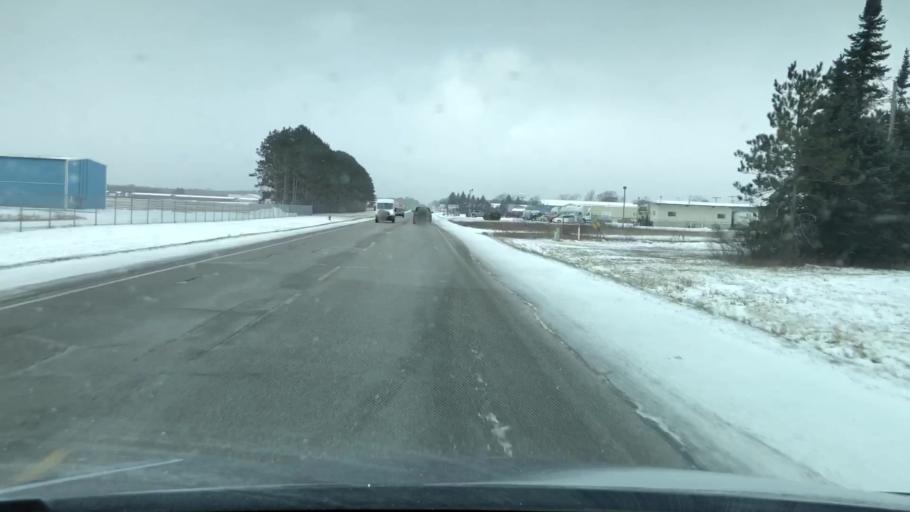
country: US
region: Michigan
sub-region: Wexford County
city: Cadillac
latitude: 44.2813
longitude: -85.4174
